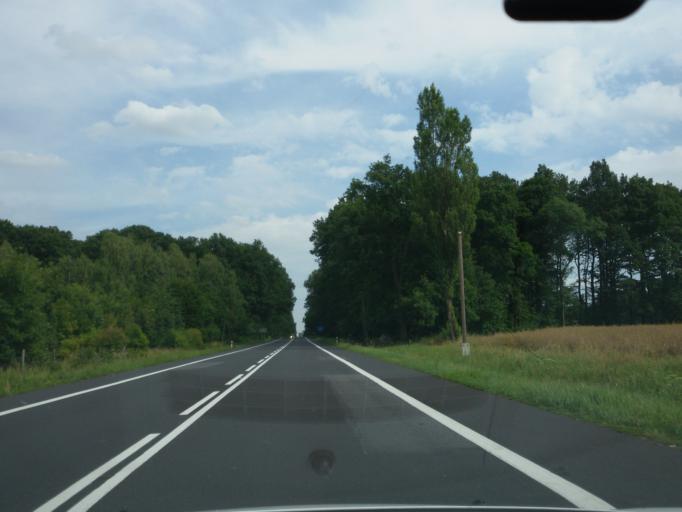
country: PL
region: Lubusz
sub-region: Powiat nowosolski
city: Bytom Odrzanski
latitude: 51.6686
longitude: 15.8022
